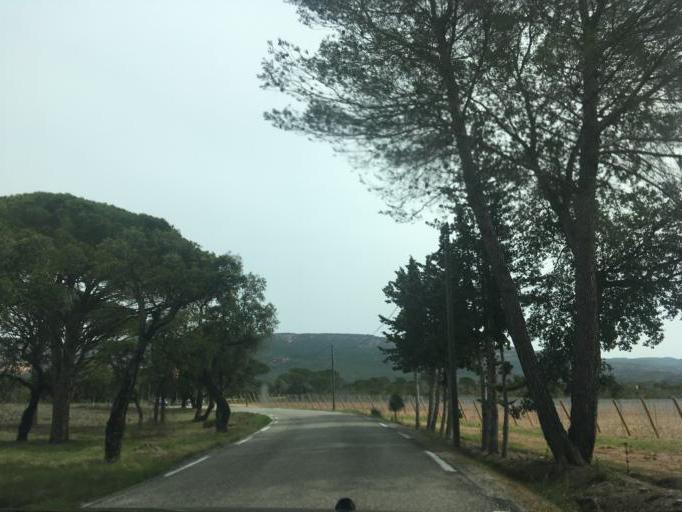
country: FR
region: Provence-Alpes-Cote d'Azur
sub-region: Departement du Var
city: Le Muy
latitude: 43.5074
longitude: 6.6012
